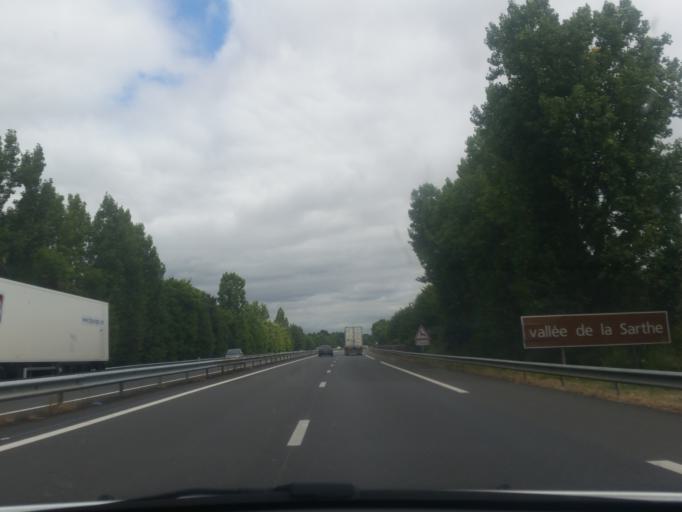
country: FR
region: Pays de la Loire
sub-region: Departement de Maine-et-Loire
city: Durtal
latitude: 47.7368
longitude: -0.2473
